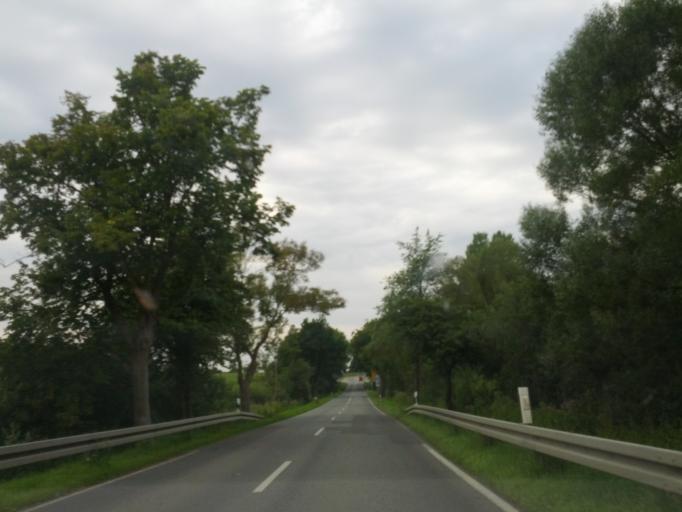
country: DE
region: Mecklenburg-Vorpommern
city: Satow-Oberhagen
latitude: 53.9725
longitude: 11.8705
